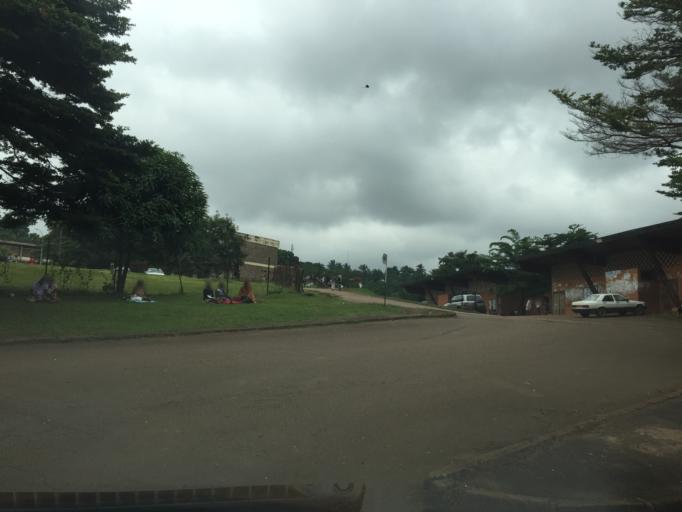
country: CM
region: Centre
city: Yaounde
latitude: 3.8581
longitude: 11.4989
